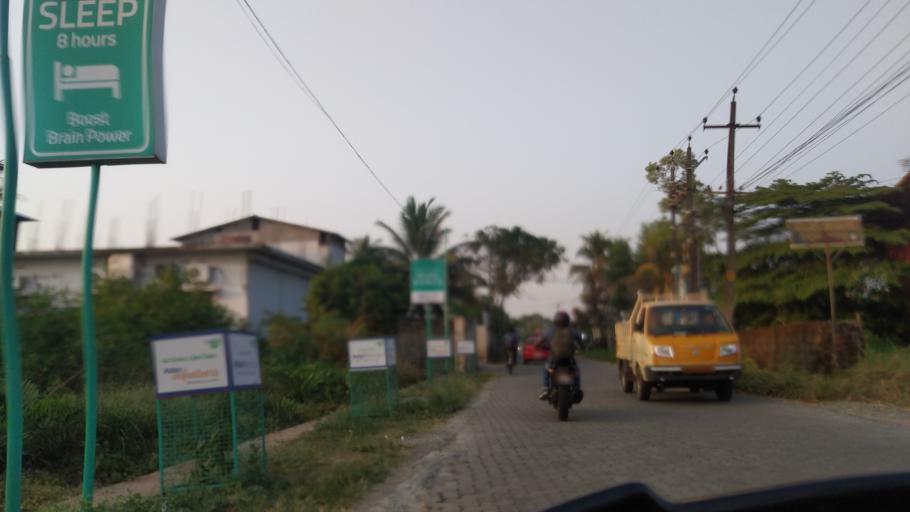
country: IN
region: Kerala
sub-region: Ernakulam
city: Elur
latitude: 10.0414
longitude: 76.2745
